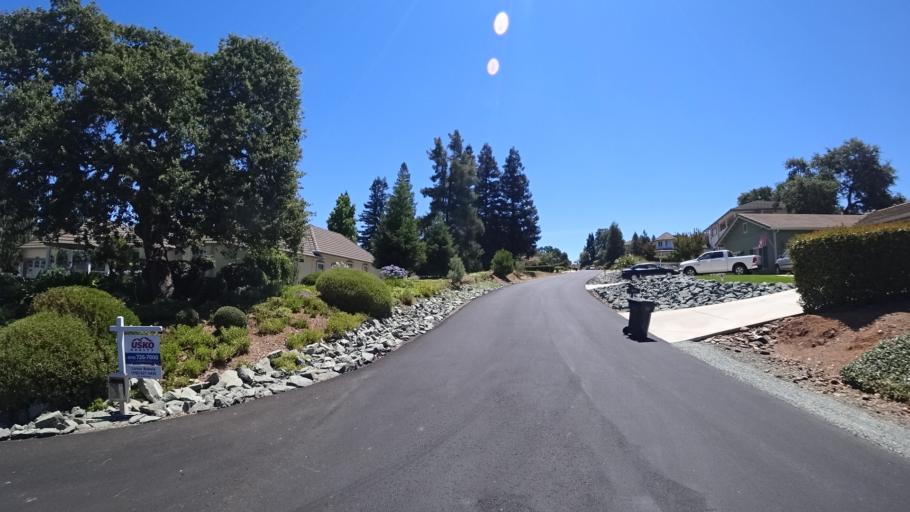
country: US
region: California
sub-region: Calaveras County
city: Valley Springs
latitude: 38.1655
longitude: -120.8290
